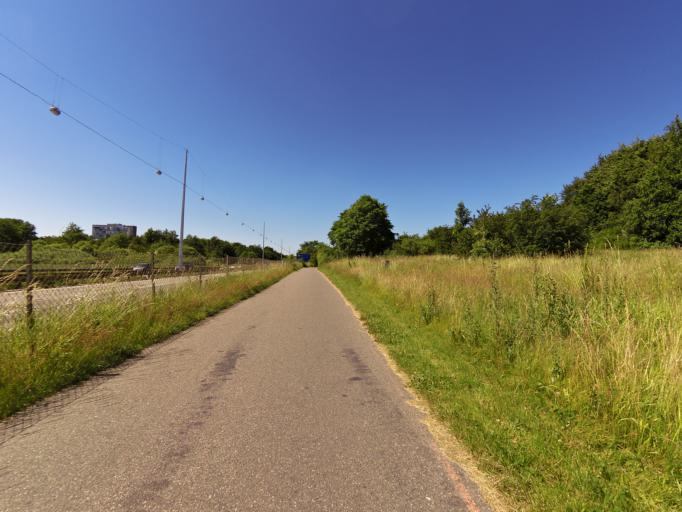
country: DK
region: Capital Region
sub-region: Gladsaxe Municipality
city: Buddinge
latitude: 55.7253
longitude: 12.4865
